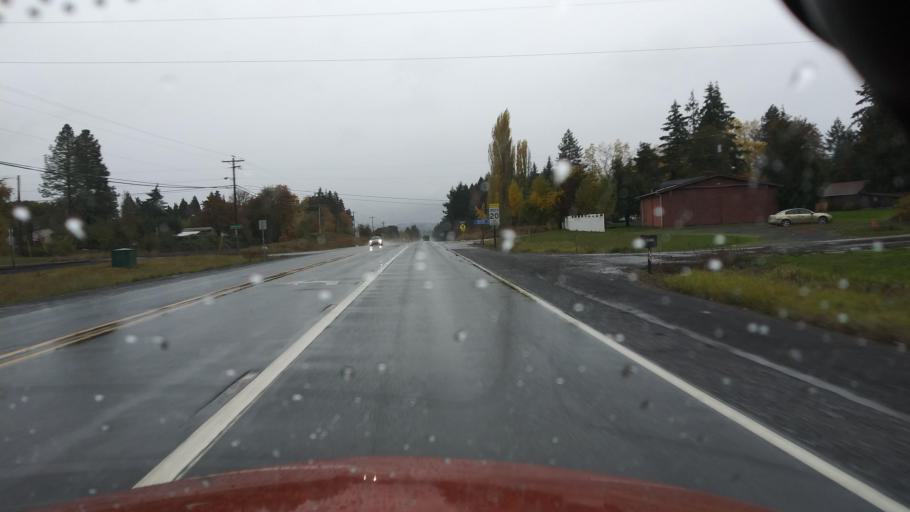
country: US
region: Oregon
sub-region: Washington County
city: Forest Grove
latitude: 45.4914
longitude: -123.1233
